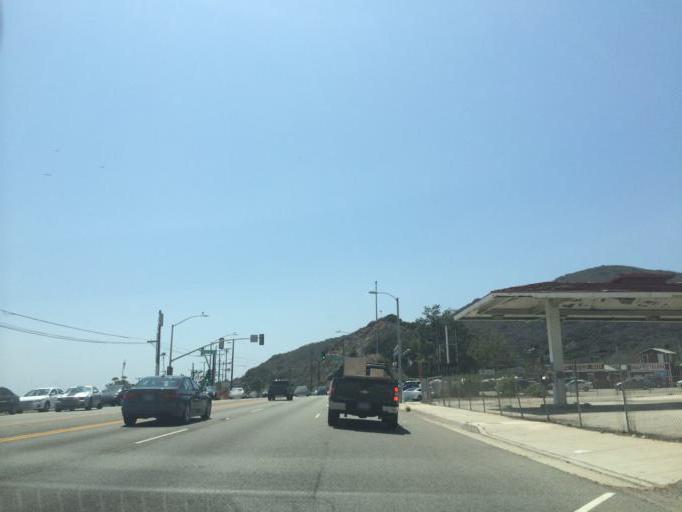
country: US
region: California
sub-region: Los Angeles County
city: Las Flores
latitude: 34.0402
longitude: -118.5784
